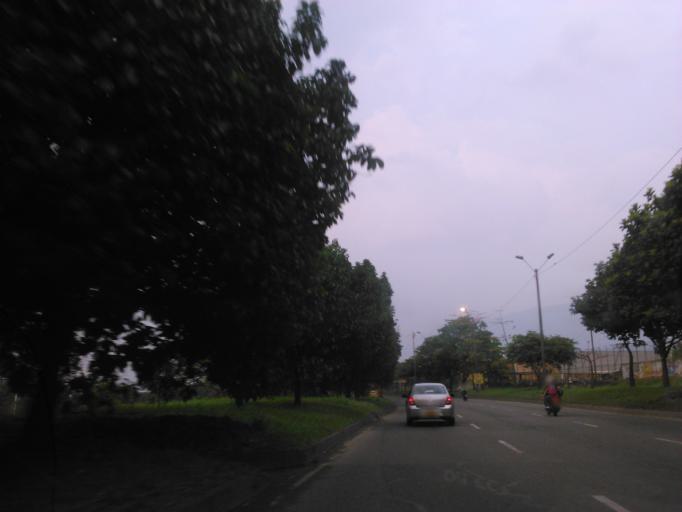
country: CO
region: Antioquia
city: Sabaneta
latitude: 6.1633
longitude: -75.6046
